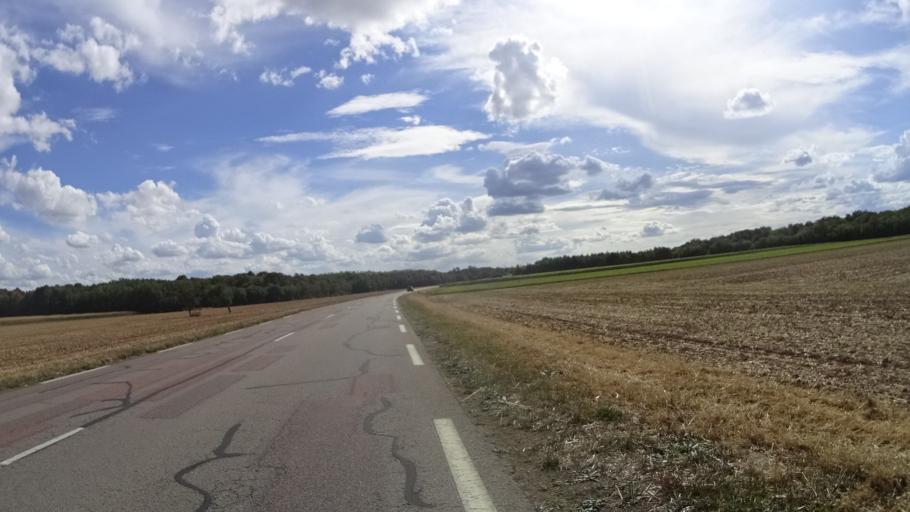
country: FR
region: Bourgogne
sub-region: Departement de la Cote-d'Or
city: Seurre
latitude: 47.0412
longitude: 5.1876
